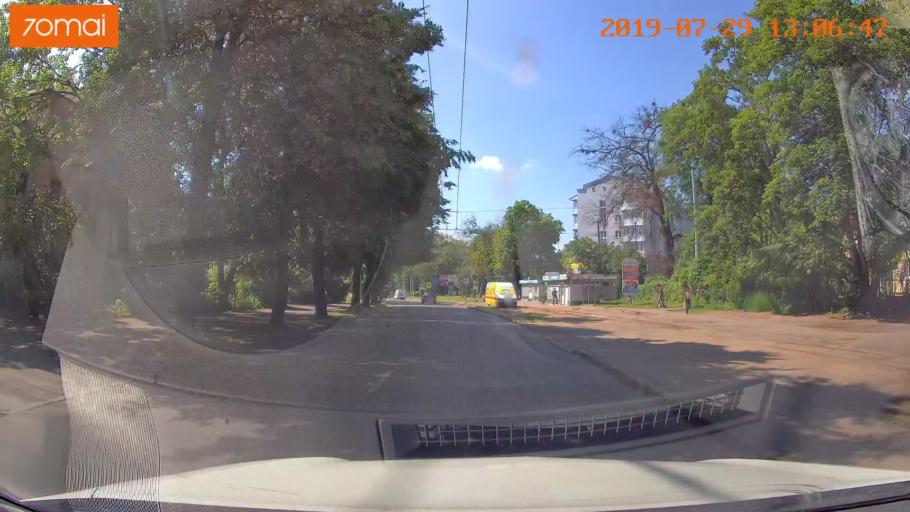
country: RU
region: Kaliningrad
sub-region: Gorod Kaliningrad
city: Kaliningrad
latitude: 54.7132
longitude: 20.4523
